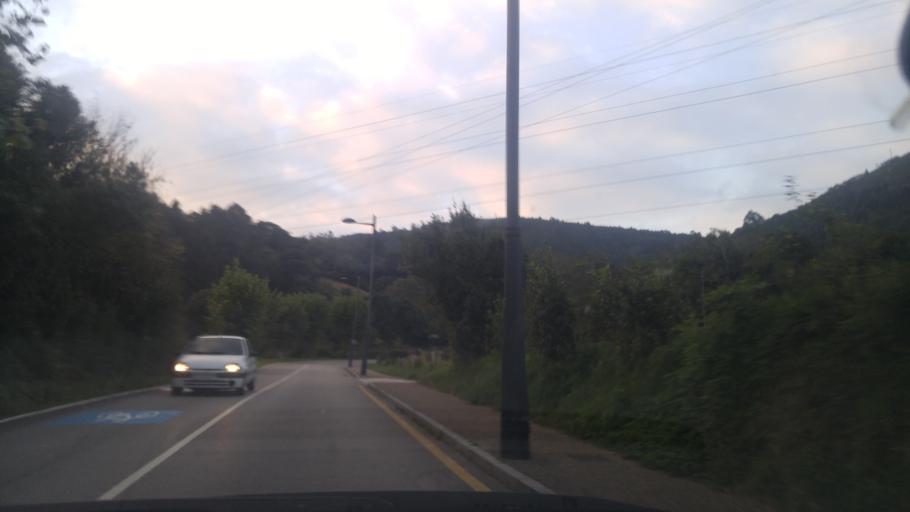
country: ES
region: Asturias
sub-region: Province of Asturias
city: Oviedo
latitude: 43.3768
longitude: -5.8660
